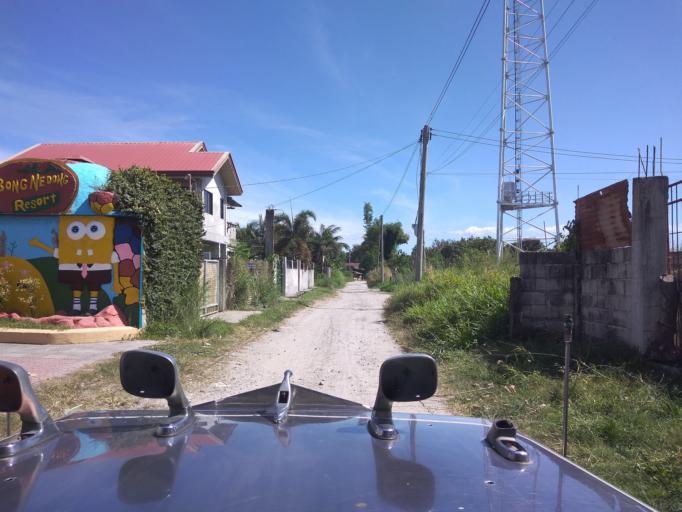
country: PH
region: Central Luzon
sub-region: Province of Pampanga
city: Magliman
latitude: 15.0374
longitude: 120.6601
